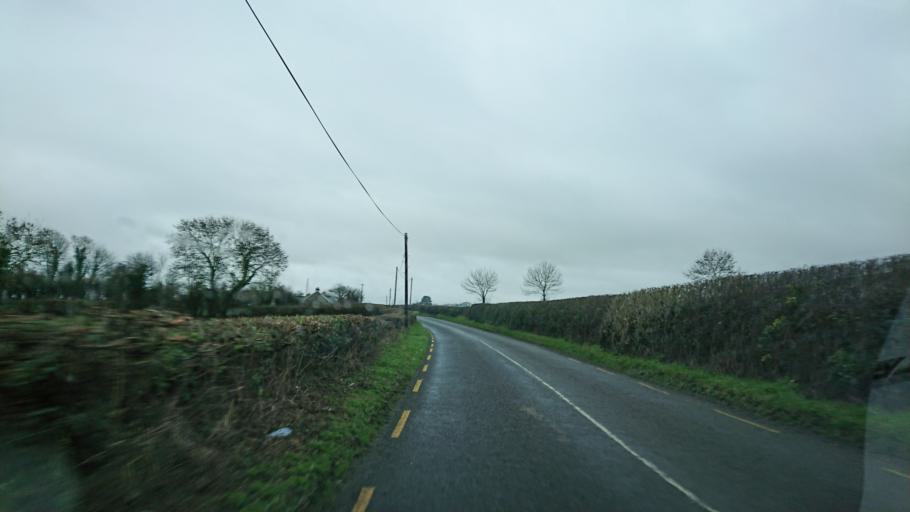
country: IE
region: Leinster
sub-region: Kilkenny
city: Callan
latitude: 52.5298
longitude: -7.2979
